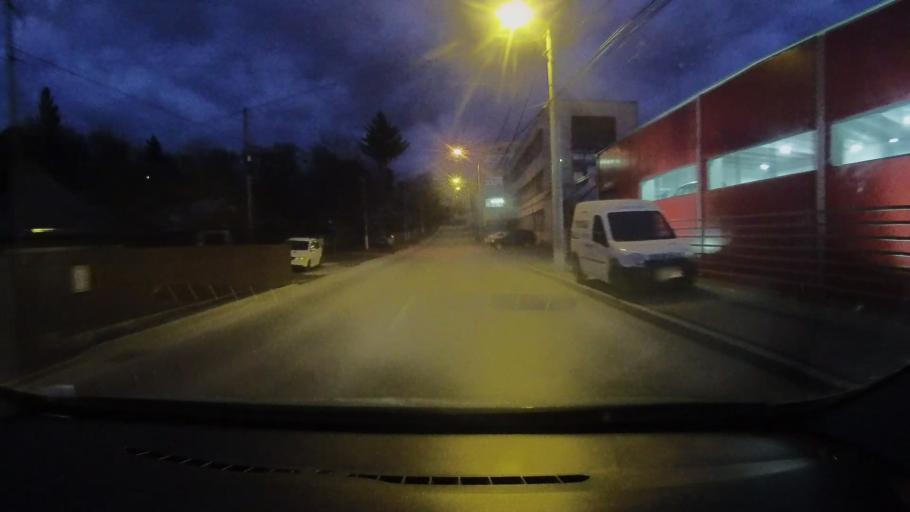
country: RO
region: Prahova
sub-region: Municipiul Campina
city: Campina
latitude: 45.1312
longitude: 25.7279
